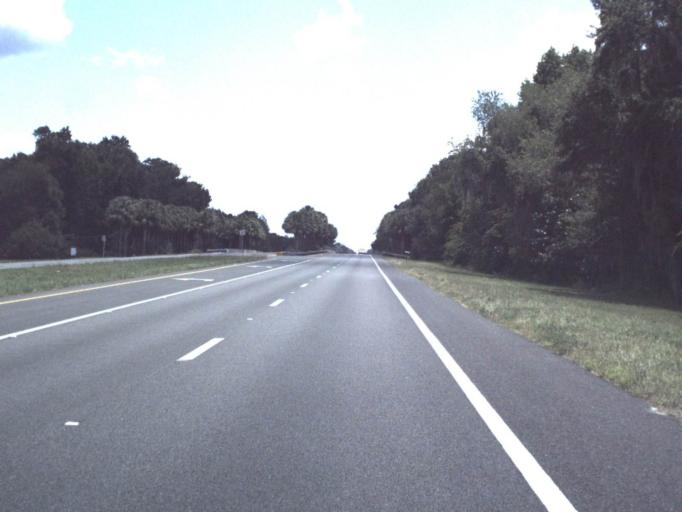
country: US
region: Florida
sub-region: Alachua County
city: Gainesville
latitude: 29.6118
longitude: -82.2509
